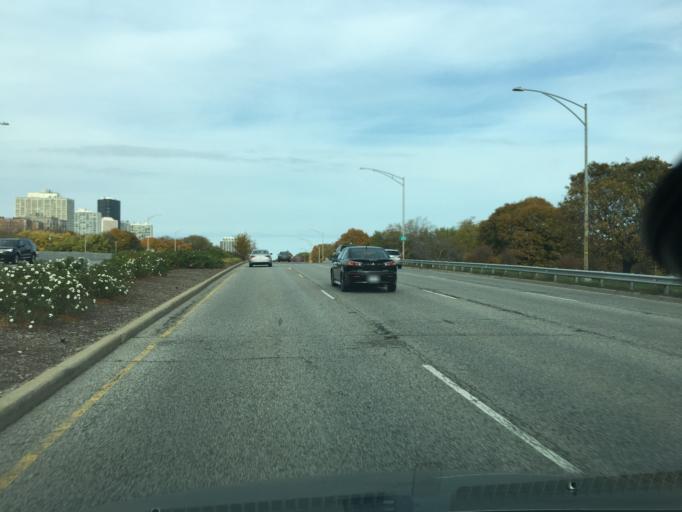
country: US
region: Illinois
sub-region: Cook County
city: Evanston
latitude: 41.9682
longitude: -87.6477
